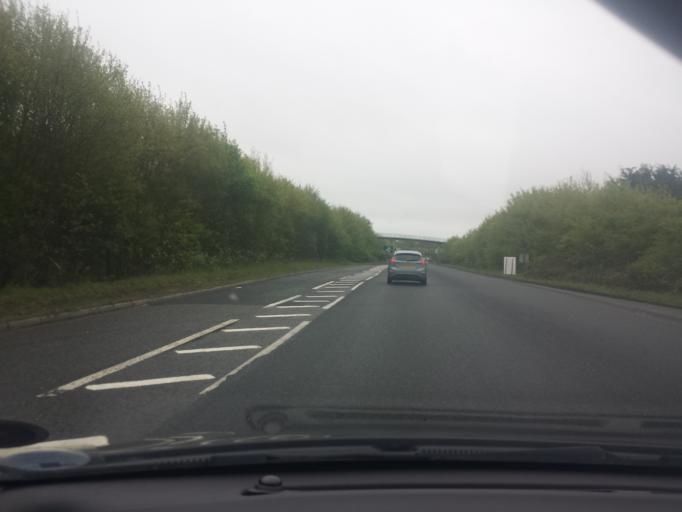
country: GB
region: England
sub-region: Essex
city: Little Clacton
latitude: 51.8232
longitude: 1.1342
